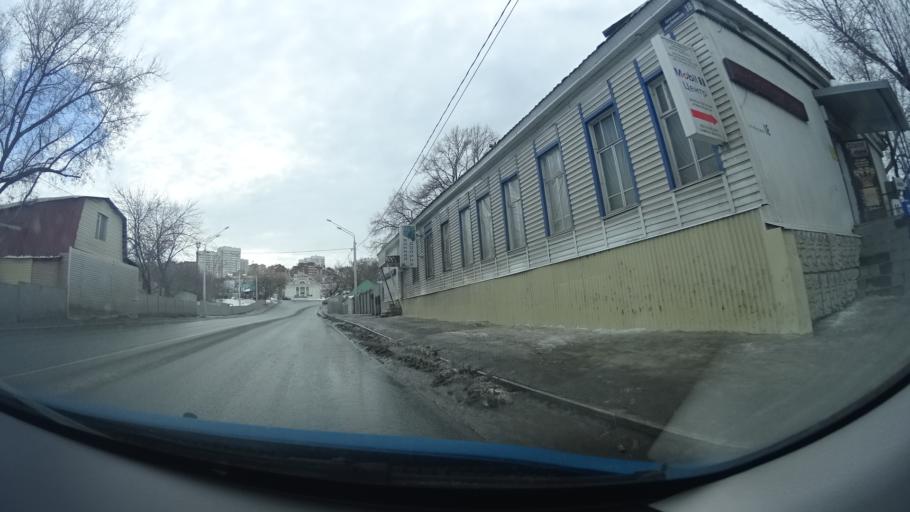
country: RU
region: Bashkortostan
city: Ufa
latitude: 54.7068
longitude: 55.9713
